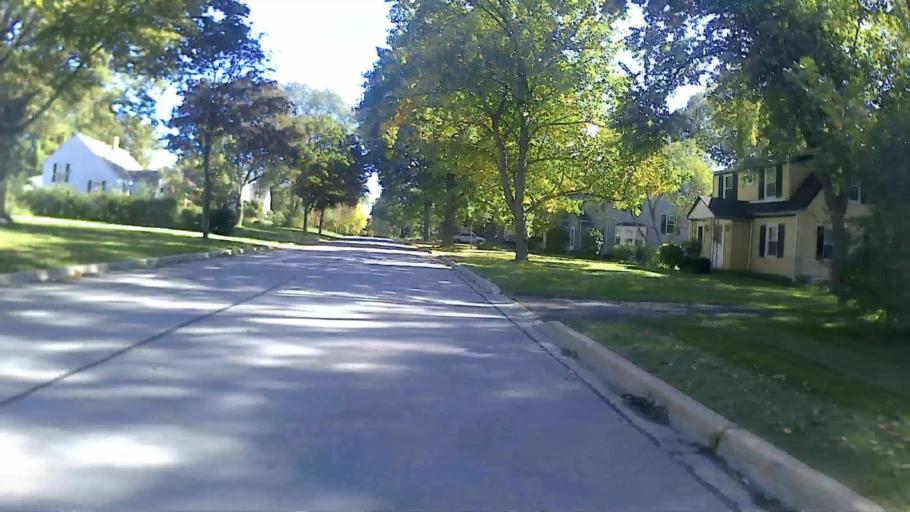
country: US
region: Illinois
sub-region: DuPage County
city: Lombard
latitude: 41.9005
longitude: -88.0245
